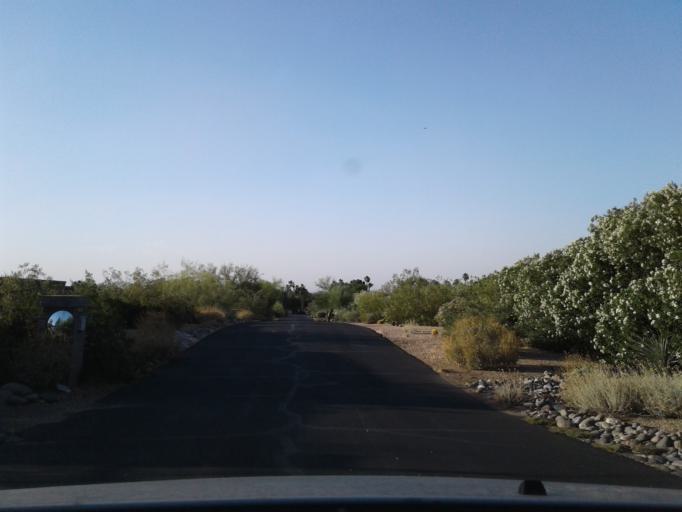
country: US
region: Arizona
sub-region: Maricopa County
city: Paradise Valley
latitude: 33.5563
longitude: -111.9539
